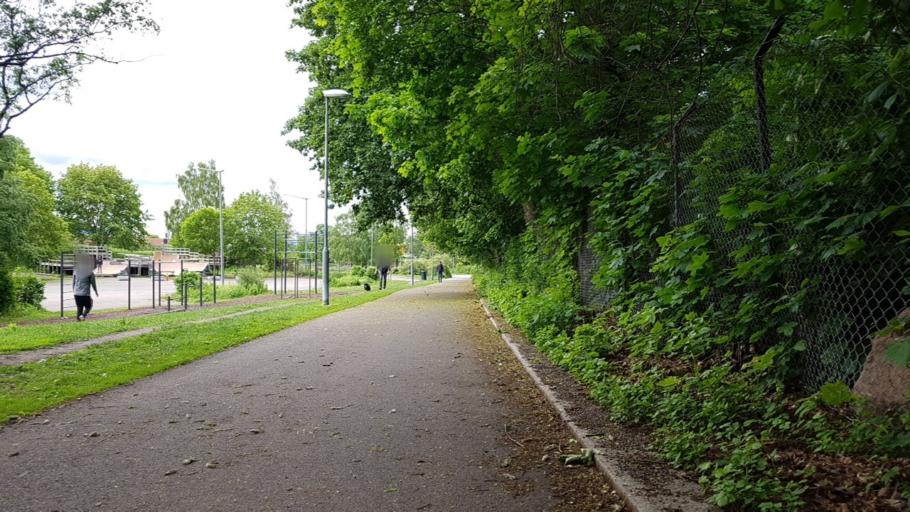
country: NO
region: Oslo
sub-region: Oslo
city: Oslo
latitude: 59.9322
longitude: 10.7730
